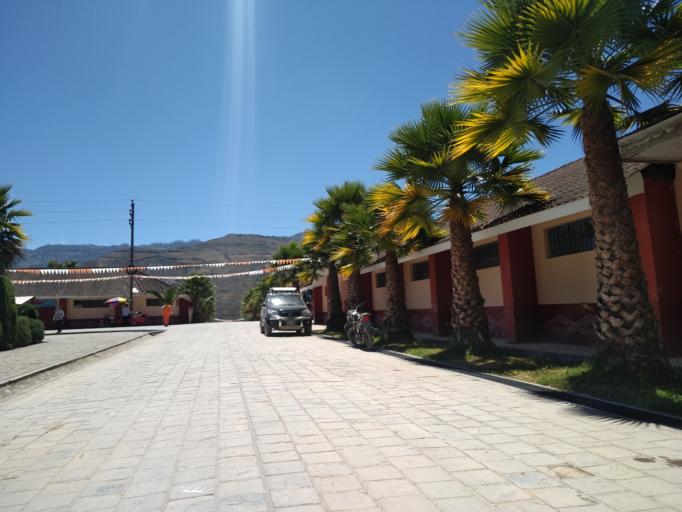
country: PE
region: Amazonas
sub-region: Provincia de Luya
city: Tingo
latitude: -6.3736
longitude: -77.9099
